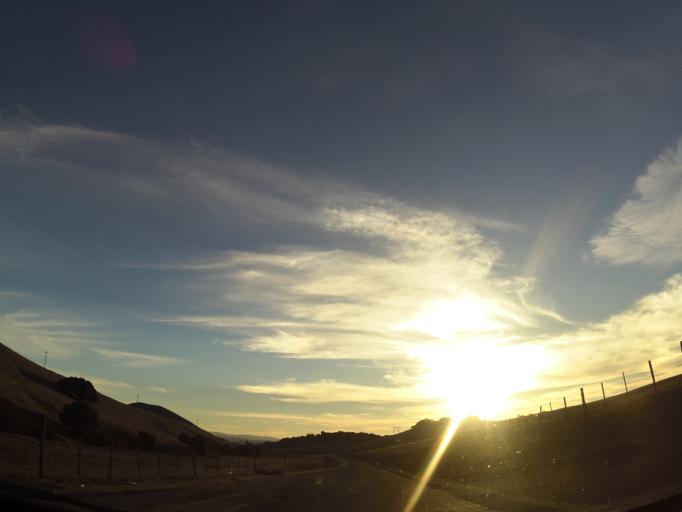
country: US
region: California
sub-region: San Benito County
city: San Juan Bautista
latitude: 36.7935
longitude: -121.5833
